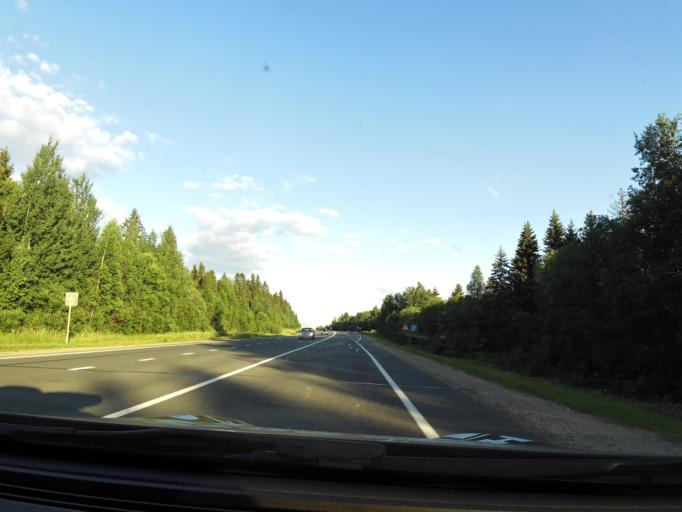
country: RU
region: Vologda
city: Vologda
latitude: 59.0817
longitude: 40.0126
